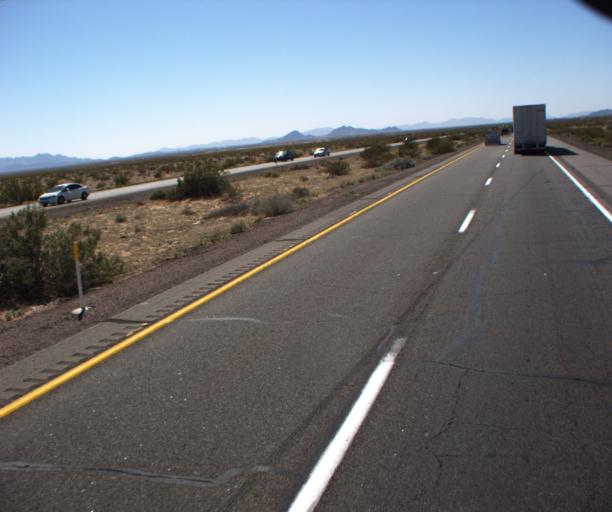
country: US
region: Arizona
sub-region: Yuma County
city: Wellton
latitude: 32.7123
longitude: -113.8307
